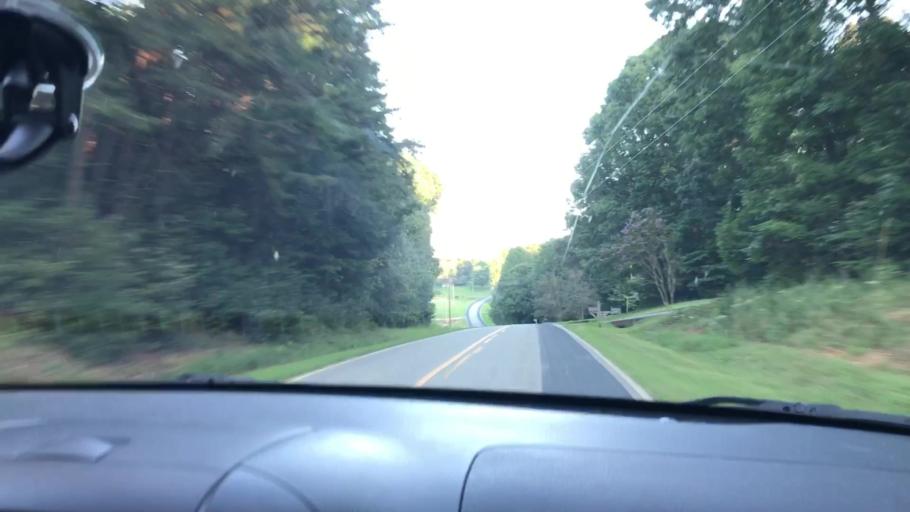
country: US
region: North Carolina
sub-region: Randolph County
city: Ramseur
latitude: 35.7833
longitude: -79.6396
